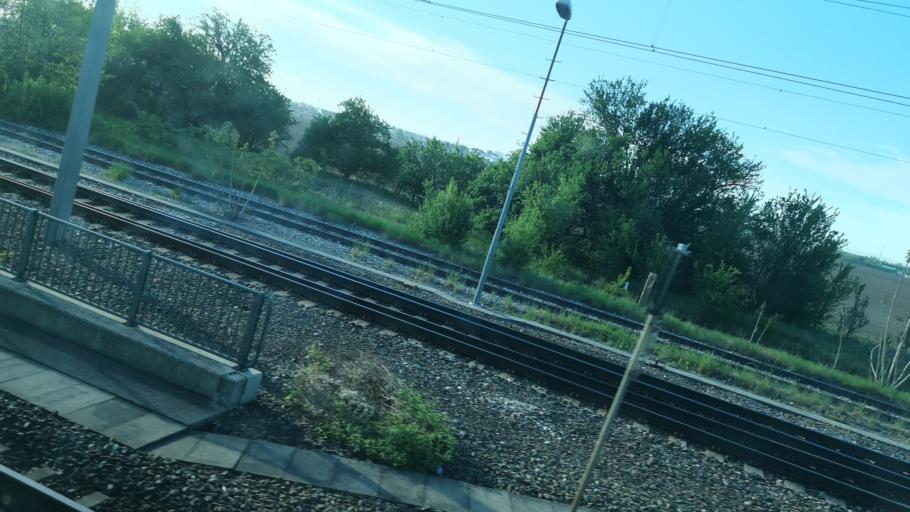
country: AT
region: Lower Austria
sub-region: Politischer Bezirk Wien-Umgebung
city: Schwechat
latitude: 48.1391
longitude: 16.4530
